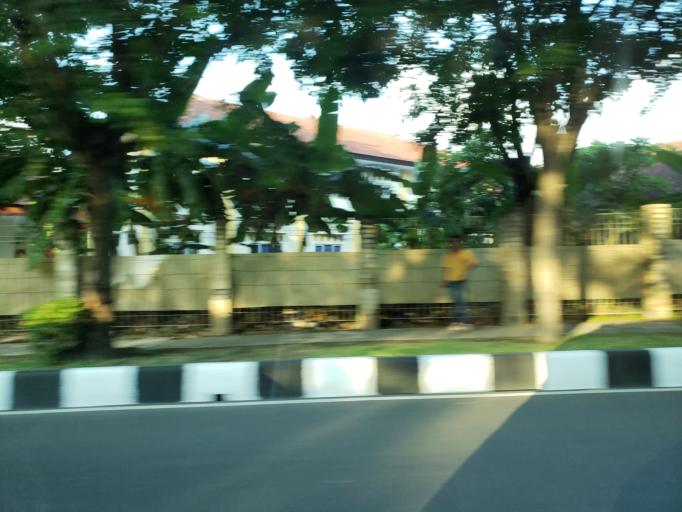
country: ID
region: Bali
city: Kelanabian
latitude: -8.7442
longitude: 115.1769
